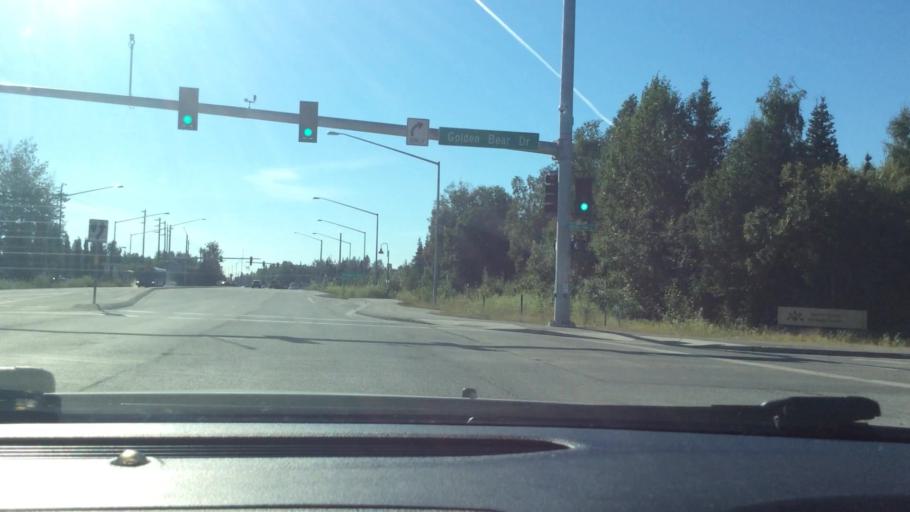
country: US
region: Alaska
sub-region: Anchorage Municipality
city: Elmendorf Air Force Base
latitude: 61.2311
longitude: -149.7370
